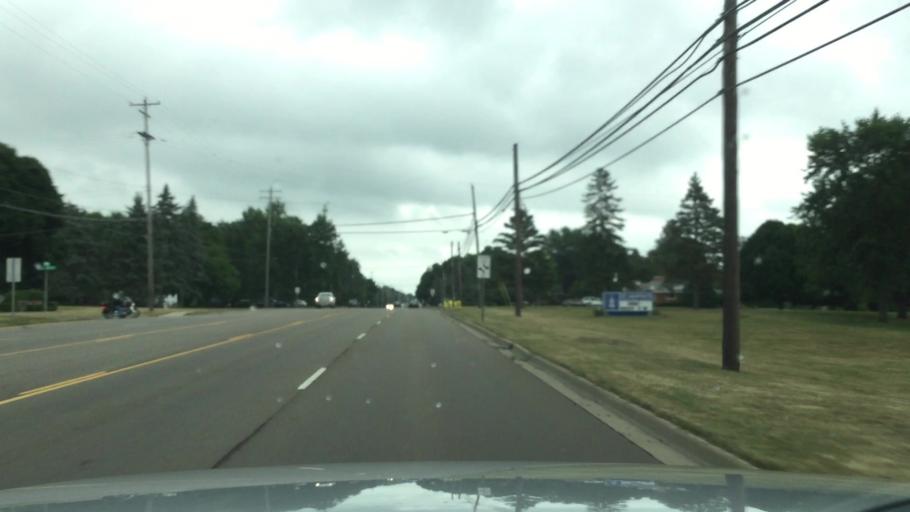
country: US
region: Michigan
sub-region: Genesee County
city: Davison
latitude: 43.0341
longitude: -83.5498
